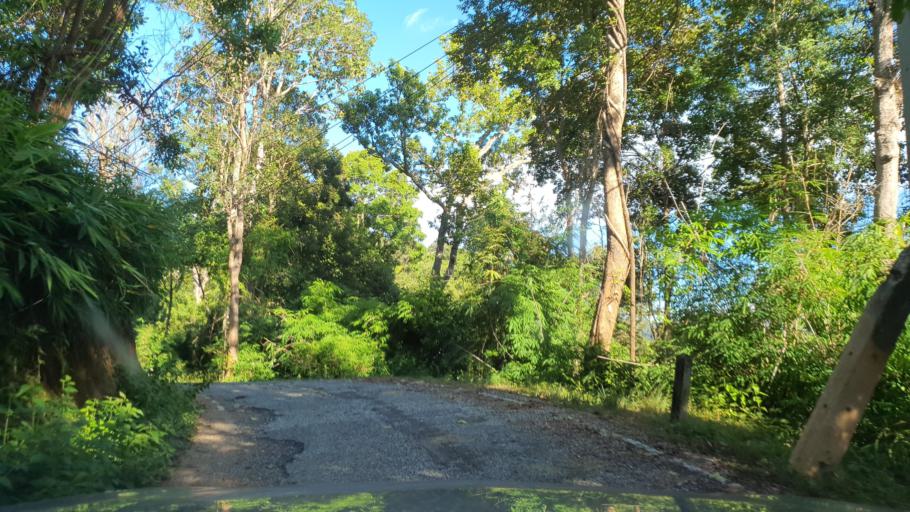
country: TH
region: Chiang Mai
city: Mae On
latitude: 18.8143
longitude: 99.3234
